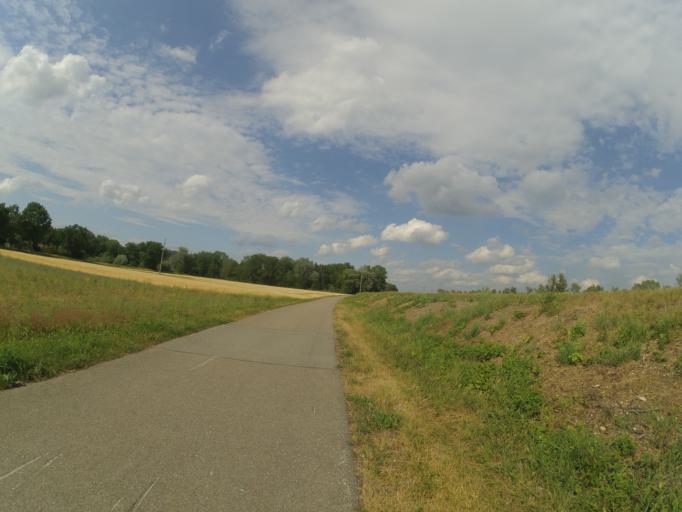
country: DE
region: Baden-Wuerttemberg
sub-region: Tuebingen Region
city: Ersingen
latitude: 48.3080
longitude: 9.8686
